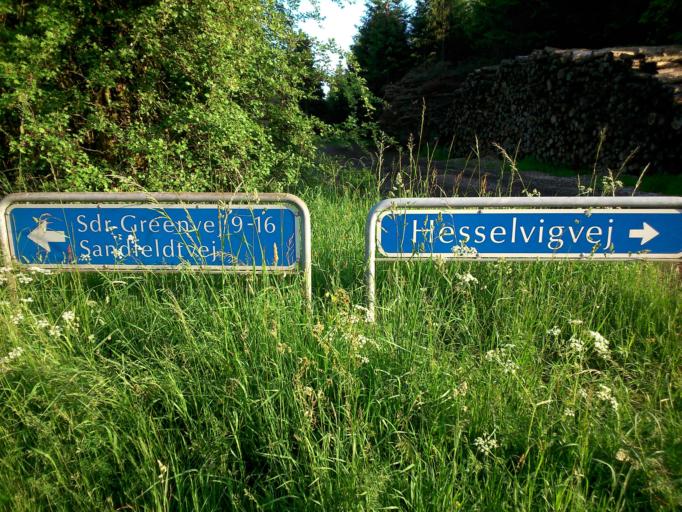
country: DK
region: Central Jutland
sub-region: Herning Kommune
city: Lind
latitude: 55.9904
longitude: 8.9645
